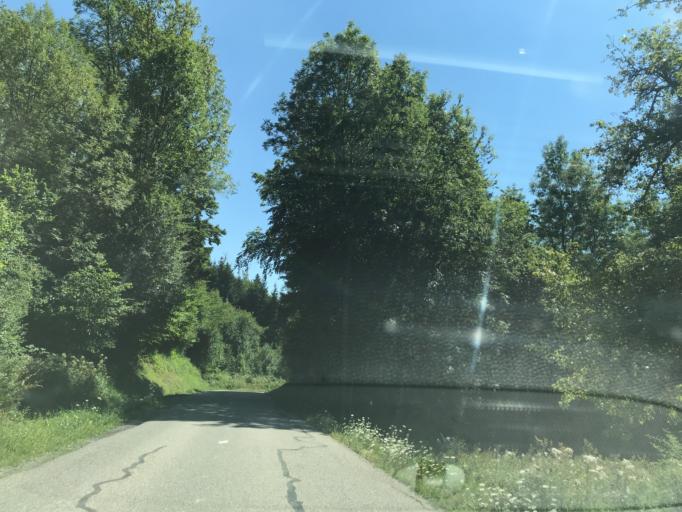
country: FR
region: Rhone-Alpes
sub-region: Departement de la Haute-Savoie
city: Thorens-Glieres
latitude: 45.9706
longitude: 6.2186
